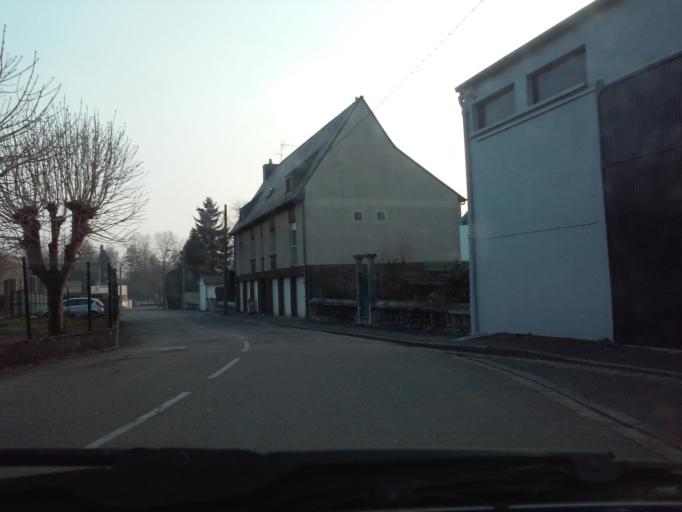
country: FR
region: Brittany
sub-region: Departement d'Ille-et-Vilaine
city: Fougeres
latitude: 48.3472
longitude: -1.1951
